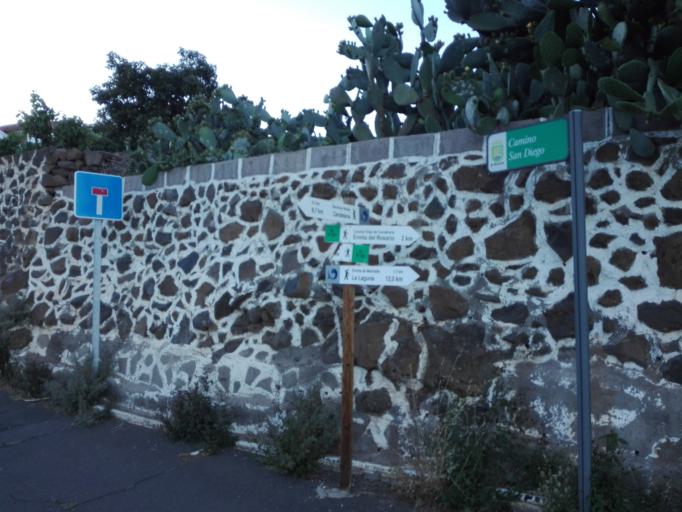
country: ES
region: Canary Islands
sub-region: Provincia de Santa Cruz de Tenerife
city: Candelaria
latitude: 28.4035
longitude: -16.3607
